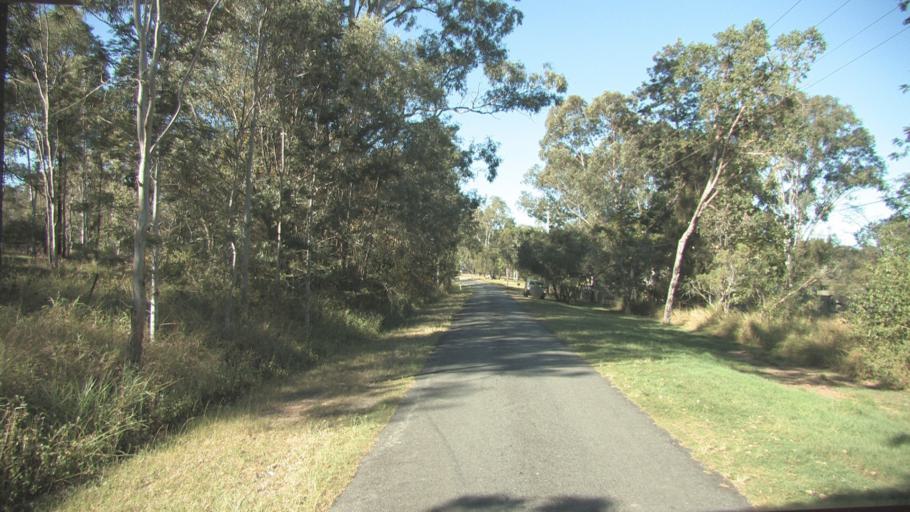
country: AU
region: Queensland
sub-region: Logan
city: North Maclean
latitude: -27.7671
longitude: 153.0277
